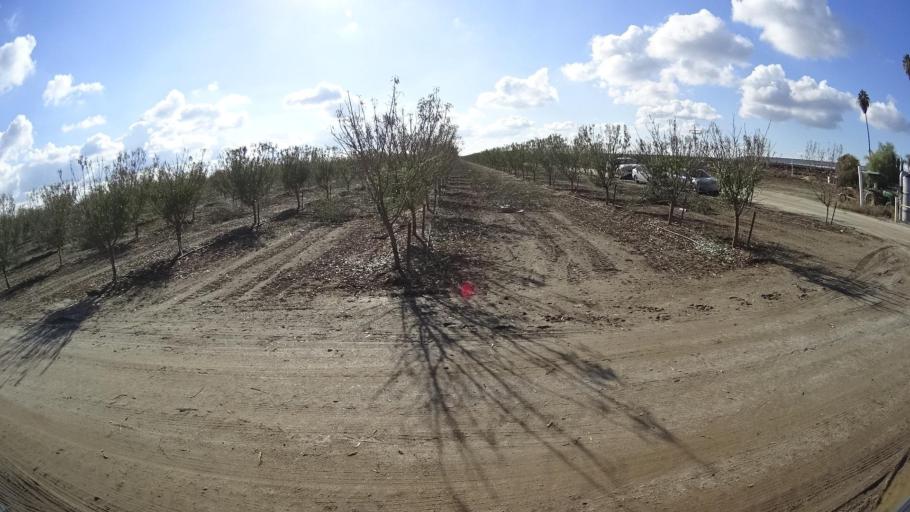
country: US
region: California
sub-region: Kern County
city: McFarland
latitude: 35.6599
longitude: -119.2365
